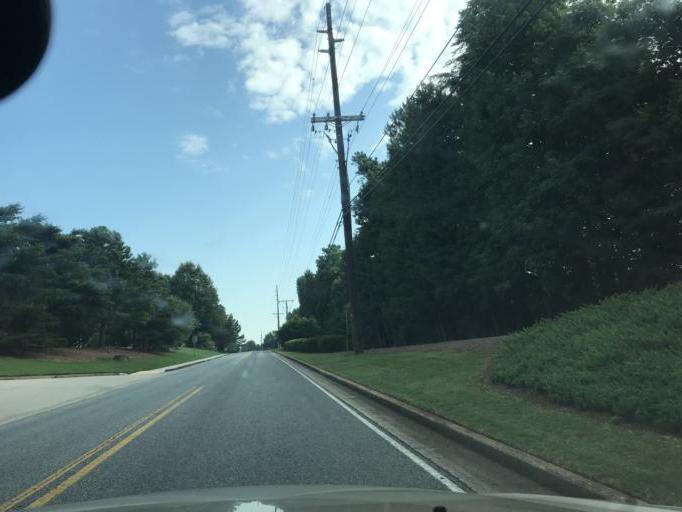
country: US
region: Georgia
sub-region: Fulton County
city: Johns Creek
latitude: 34.0639
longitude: -84.1532
